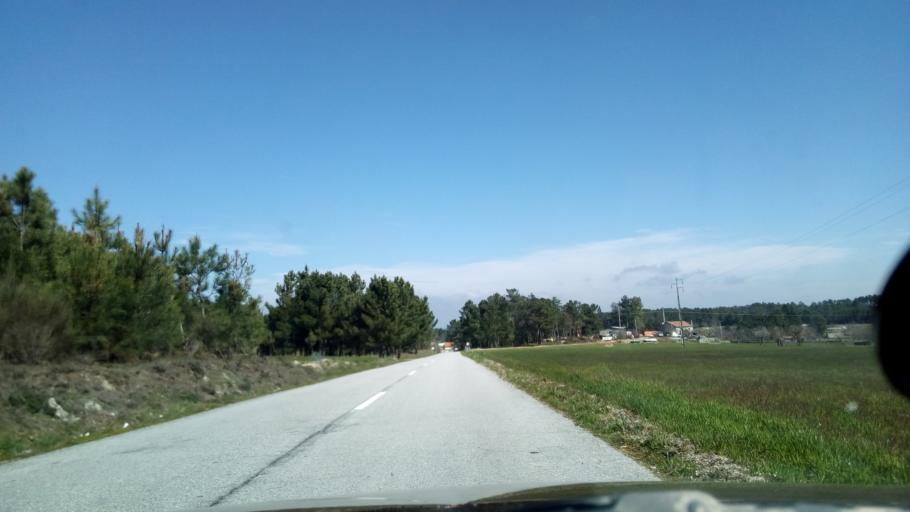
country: PT
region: Guarda
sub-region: Fornos de Algodres
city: Fornos de Algodres
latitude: 40.6420
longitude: -7.5315
